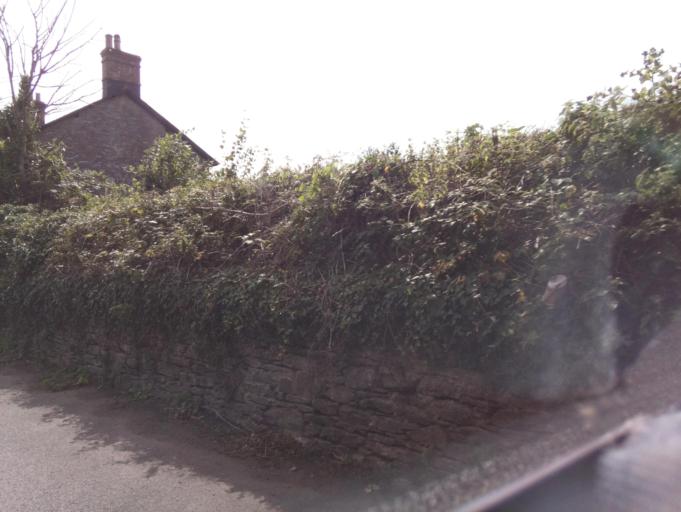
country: GB
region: England
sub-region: Borough of Torbay
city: Brixham
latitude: 50.3919
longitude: -3.5482
